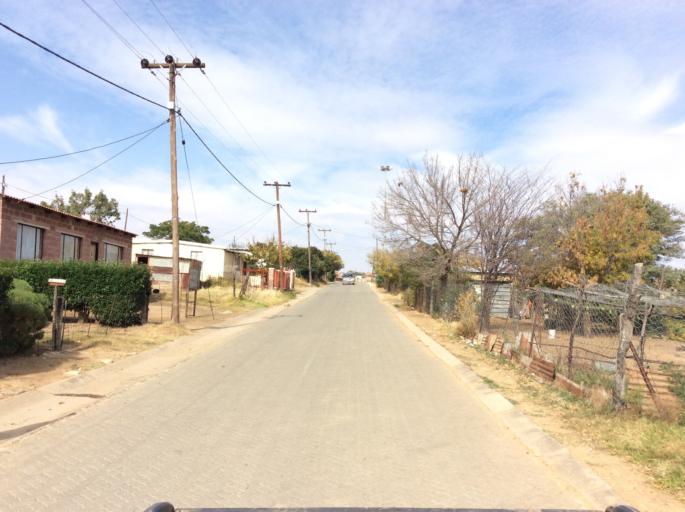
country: ZA
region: Orange Free State
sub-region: Xhariep District Municipality
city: Dewetsdorp
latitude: -29.5883
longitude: 26.6784
